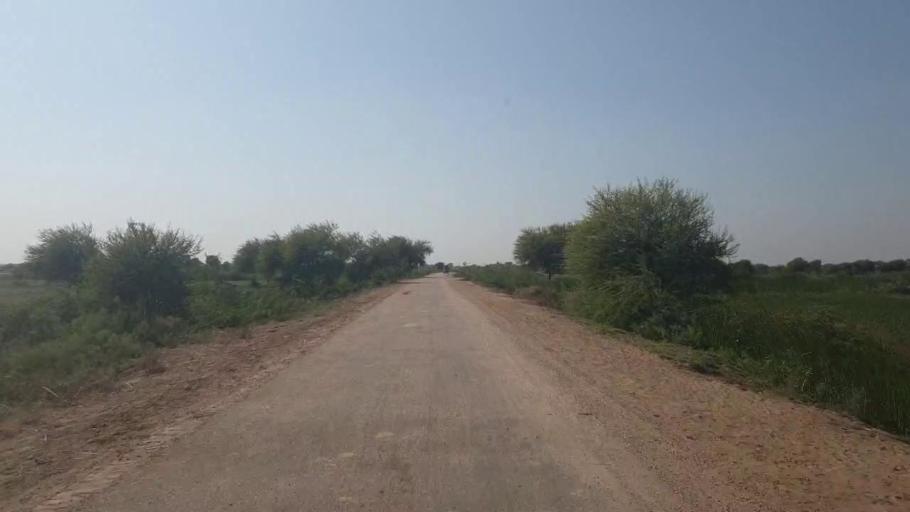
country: PK
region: Sindh
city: Badin
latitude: 24.5545
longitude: 68.8258
